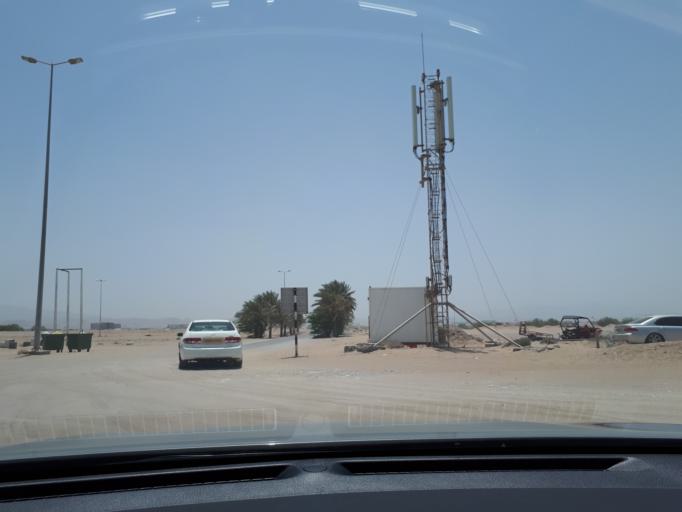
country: OM
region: Muhafazat Masqat
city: As Sib al Jadidah
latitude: 23.6328
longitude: 58.2602
